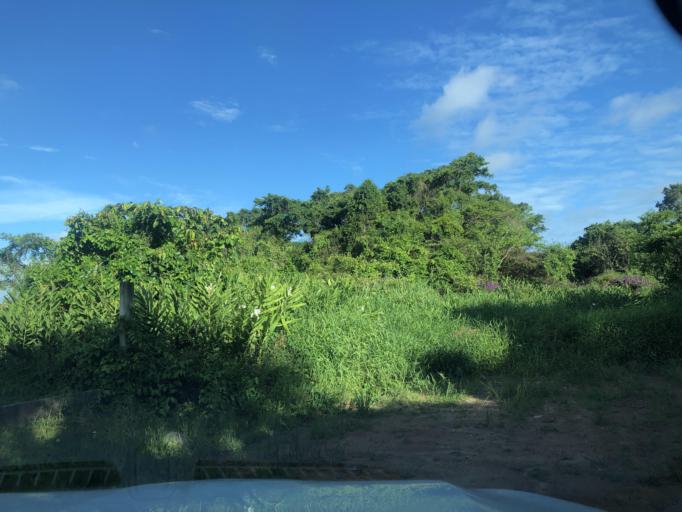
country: BR
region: Santa Catarina
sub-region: Sao Francisco Do Sul
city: Sao Francisco do Sul
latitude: -26.2126
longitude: -48.5361
